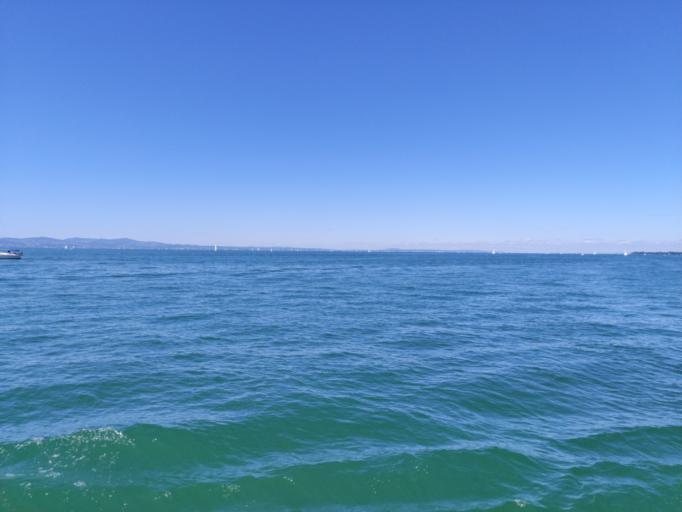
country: DE
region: Bavaria
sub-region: Swabia
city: Bodolz
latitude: 47.5532
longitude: 9.6451
